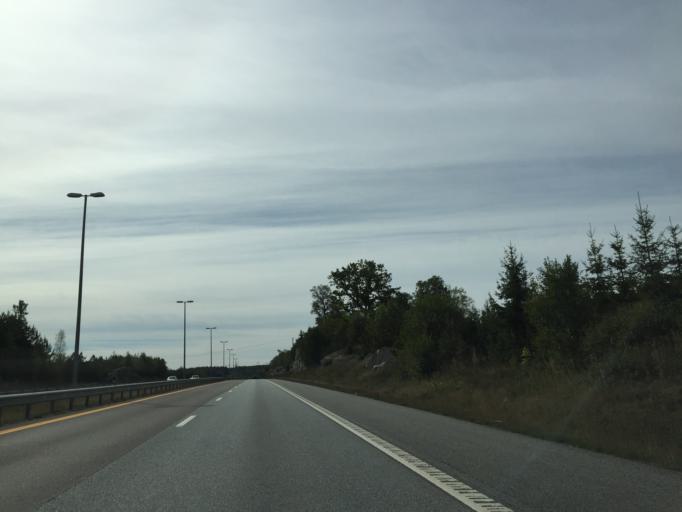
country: NO
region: Akershus
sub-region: Vestby
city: Vestby
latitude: 59.5503
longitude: 10.7227
